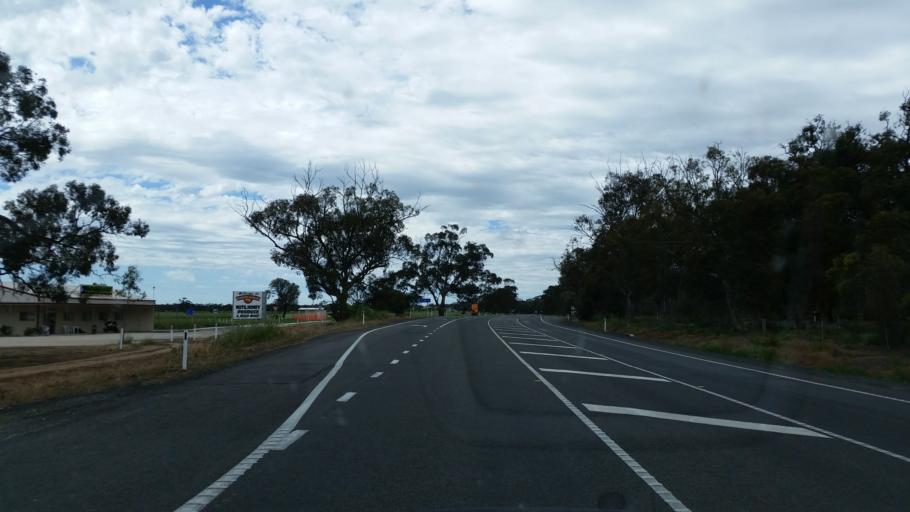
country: AU
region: South Australia
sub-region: Tatiara
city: Bordertown
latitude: -36.3441
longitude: 140.9670
